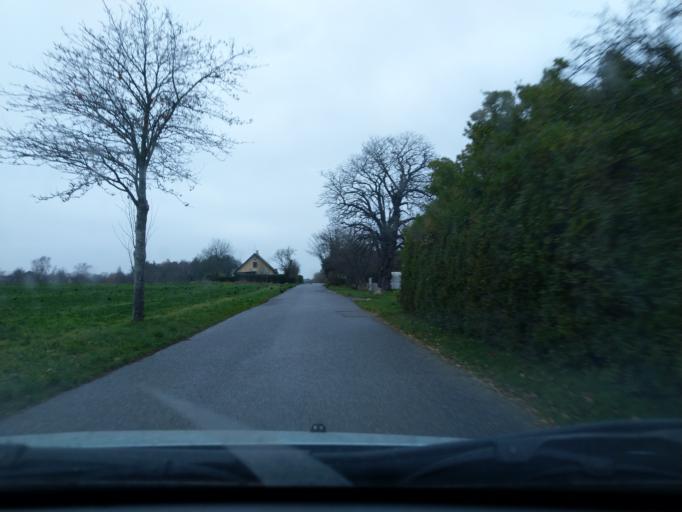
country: DK
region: Zealand
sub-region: Vordingborg Kommune
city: Praesto
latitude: 55.1181
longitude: 12.1341
